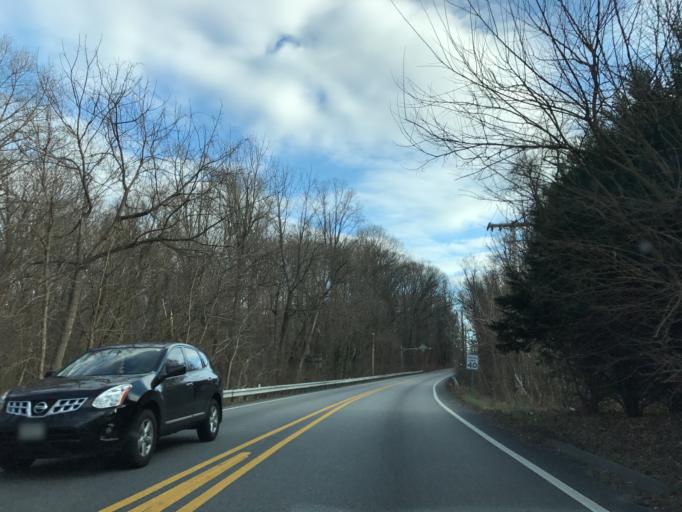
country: US
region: Maryland
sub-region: Anne Arundel County
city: Crownsville
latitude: 39.0526
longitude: -76.6182
